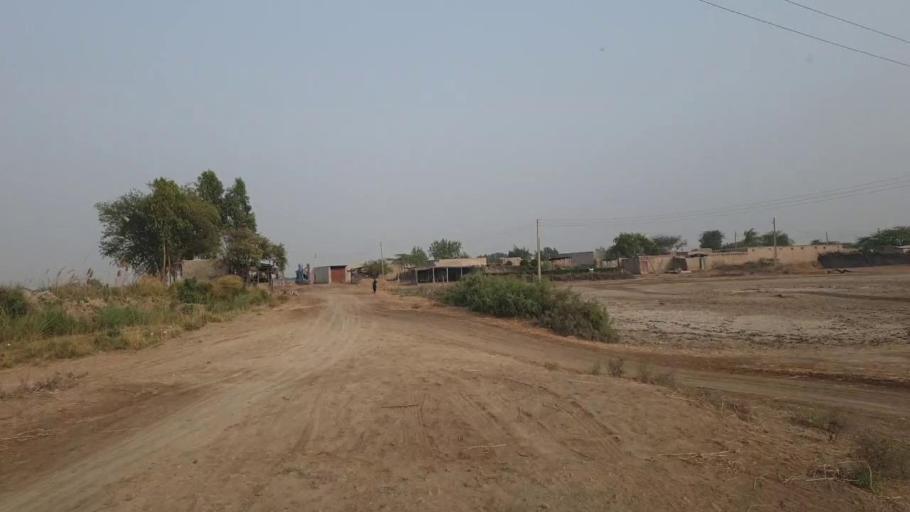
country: PK
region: Sindh
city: Mirpur Batoro
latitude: 24.5578
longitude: 68.4228
